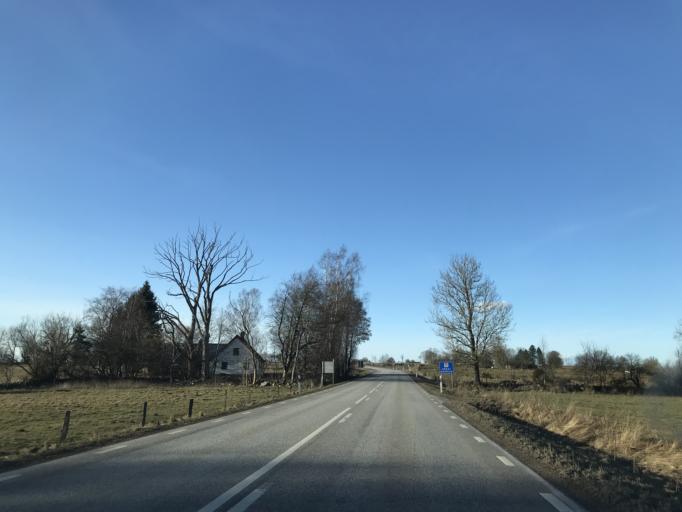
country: SE
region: Skane
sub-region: Sjobo Kommun
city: Sjoebo
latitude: 55.7389
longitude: 13.7024
